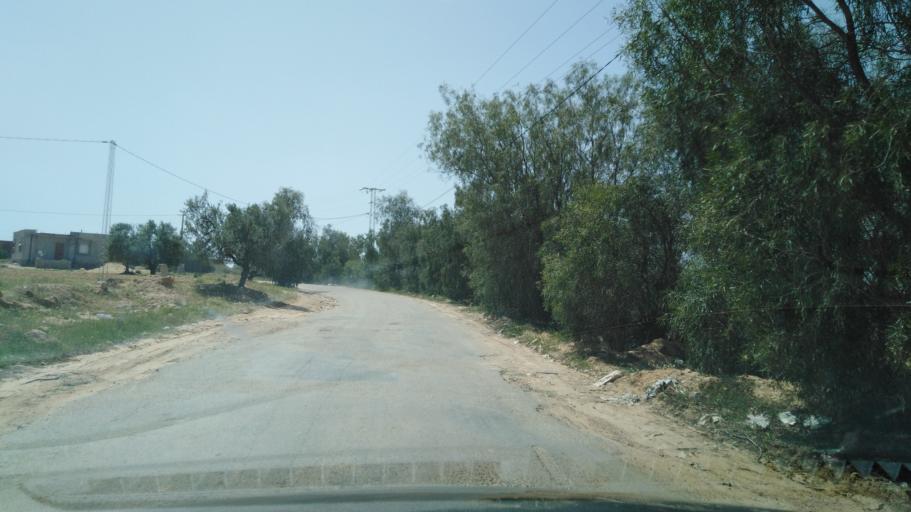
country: TN
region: Safaqis
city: Sfax
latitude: 34.7222
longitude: 10.5304
